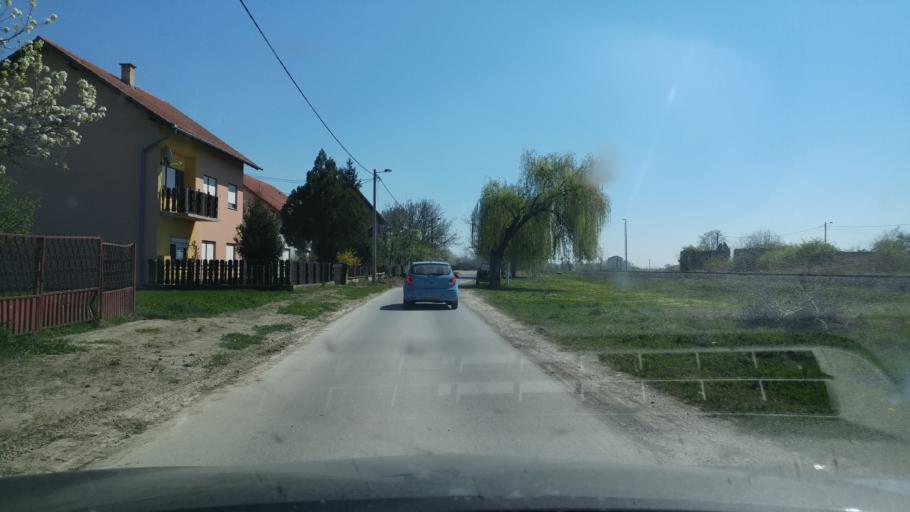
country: HR
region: Osjecko-Baranjska
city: Laslovo
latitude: 45.4128
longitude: 18.7095
